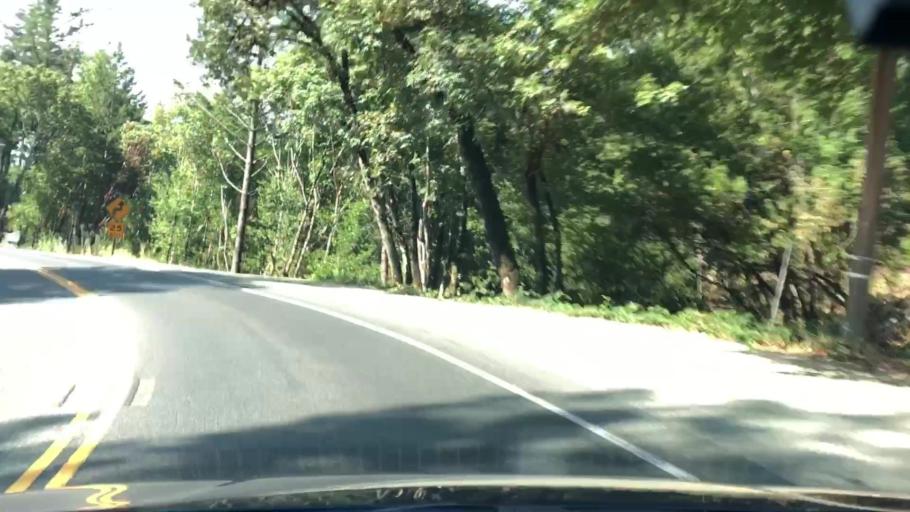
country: US
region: California
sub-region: Napa County
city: Calistoga
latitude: 38.6457
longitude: -122.5924
